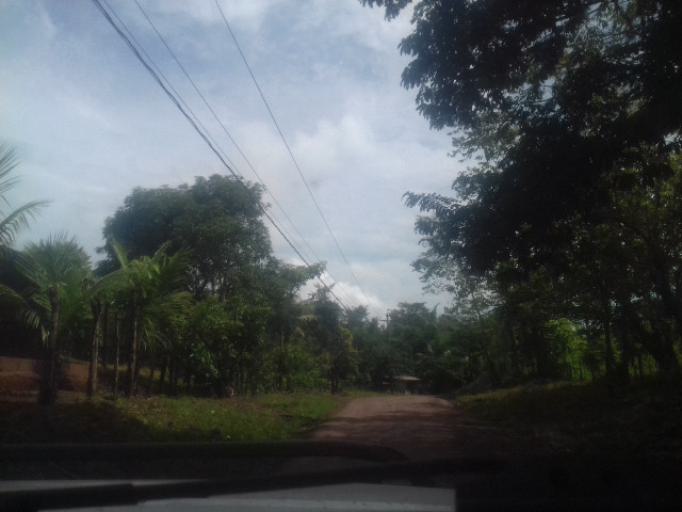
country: NI
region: Jinotega
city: San Jose de Bocay
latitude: 13.5102
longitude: -85.2526
